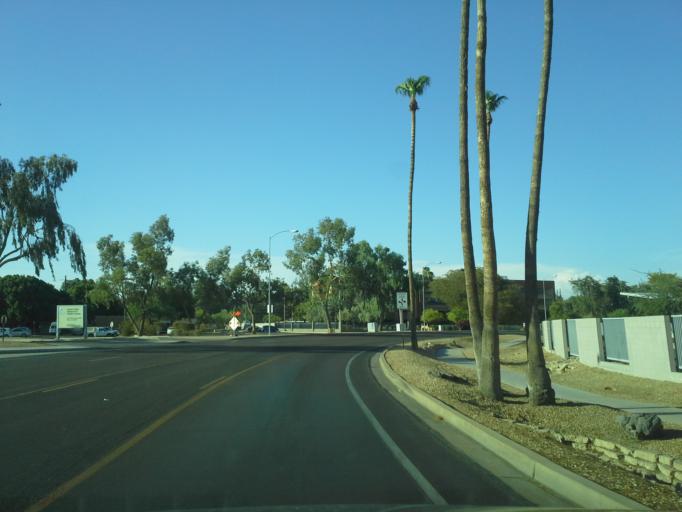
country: US
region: Arizona
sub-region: Maricopa County
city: Mesa
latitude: 33.4341
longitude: -111.8445
